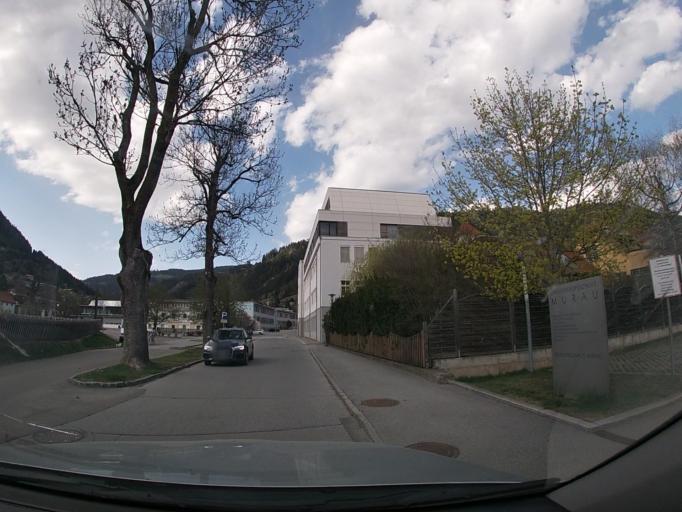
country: AT
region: Styria
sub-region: Politischer Bezirk Murau
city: Murau
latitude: 47.1115
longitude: 14.1745
